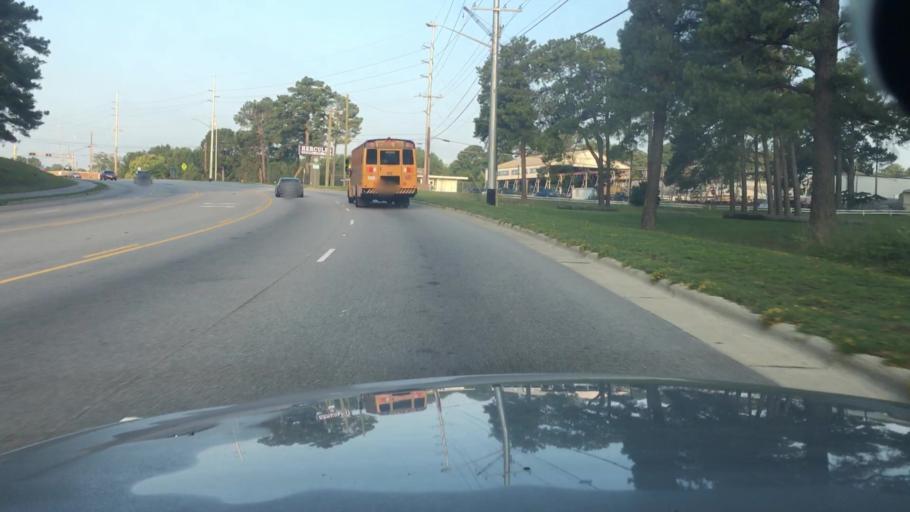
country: US
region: North Carolina
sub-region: Cumberland County
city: Fayetteville
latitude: 35.1003
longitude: -78.9125
